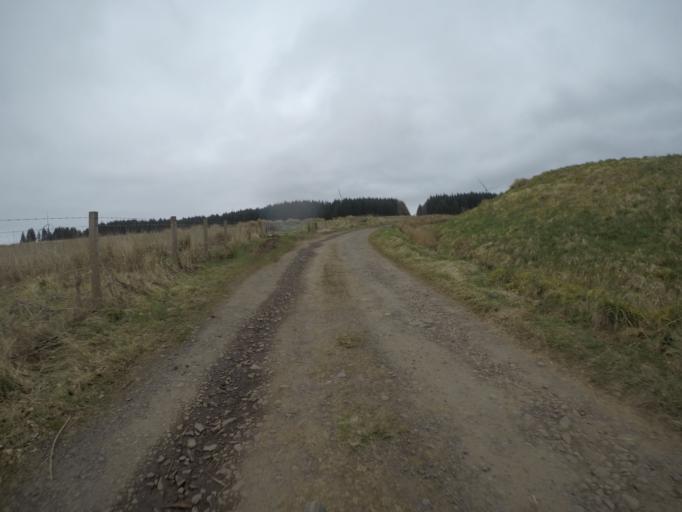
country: GB
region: Scotland
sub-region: East Ayrshire
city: Newmilns
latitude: 55.6604
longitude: -4.3443
